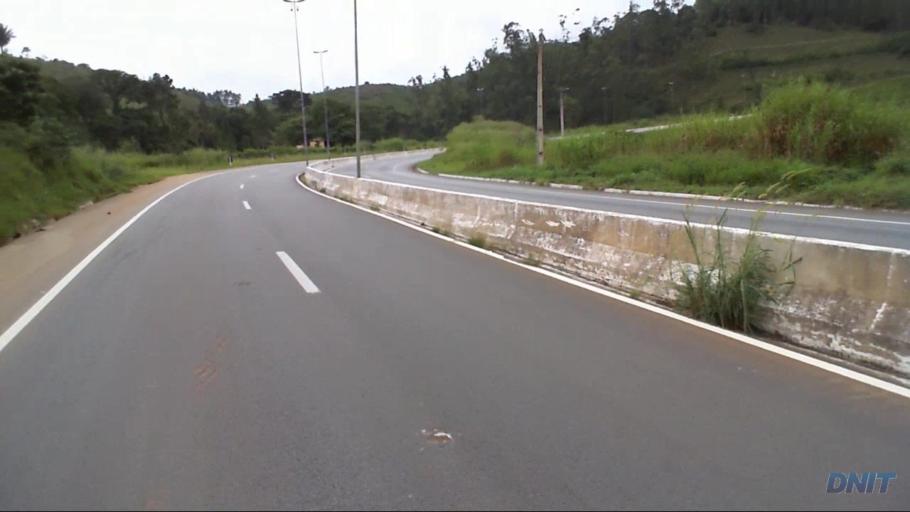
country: BR
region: Minas Gerais
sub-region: Nova Era
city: Nova Era
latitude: -19.7634
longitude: -43.0480
